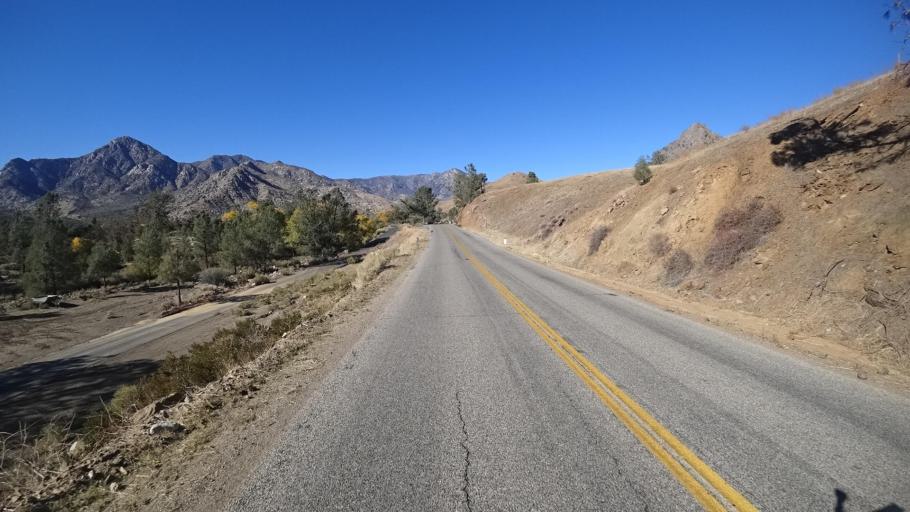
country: US
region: California
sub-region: Kern County
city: Kernville
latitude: 35.7791
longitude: -118.4385
